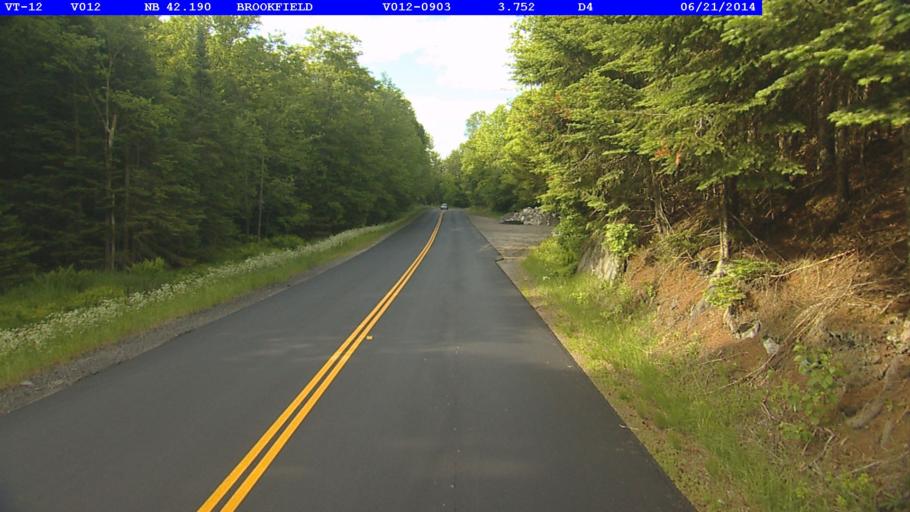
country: US
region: Vermont
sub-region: Washington County
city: Northfield
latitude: 44.0557
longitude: -72.6397
